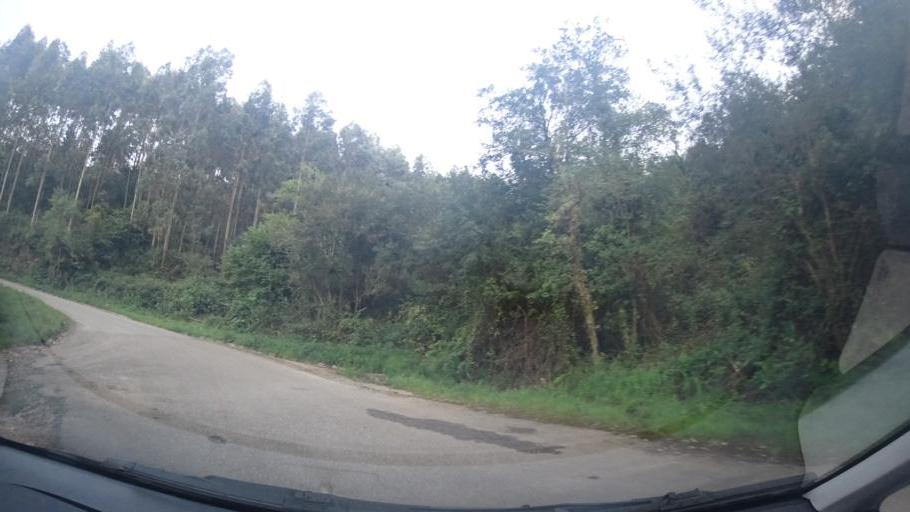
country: ES
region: Asturias
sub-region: Province of Asturias
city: Colunga
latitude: 43.4537
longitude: -5.2087
